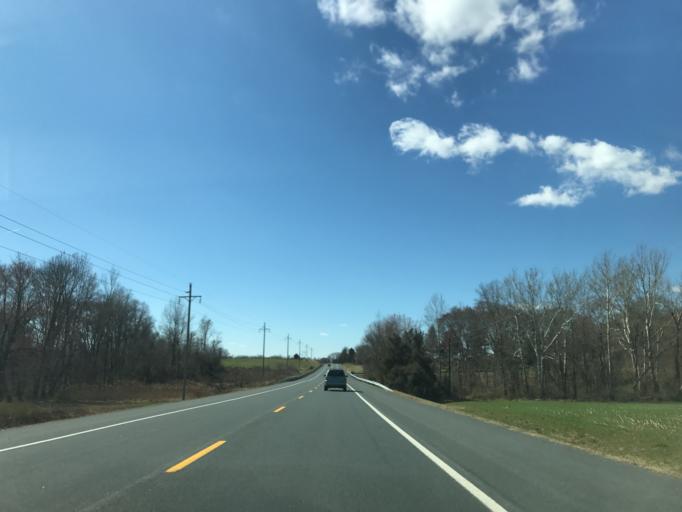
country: US
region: Maryland
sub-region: Queen Anne's County
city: Kingstown
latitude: 39.2564
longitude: -75.9820
